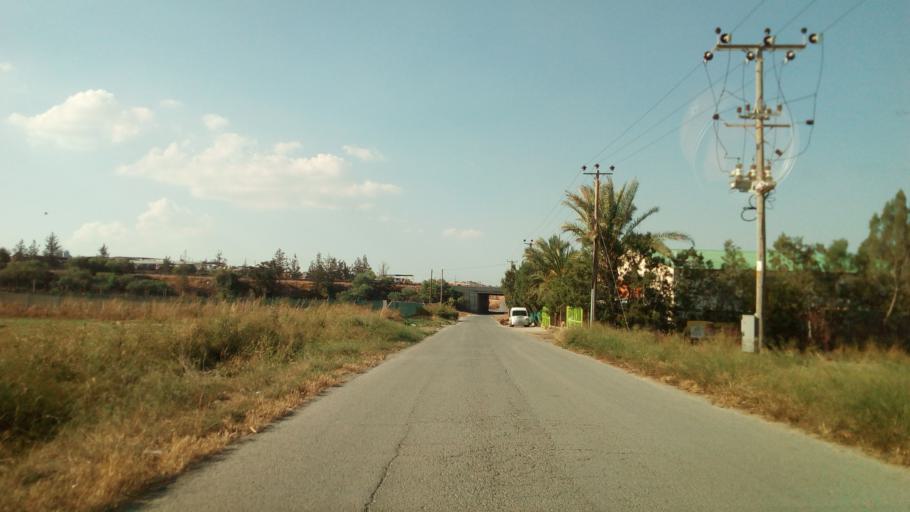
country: CY
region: Larnaka
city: Aradippou
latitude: 34.9612
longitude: 33.5937
